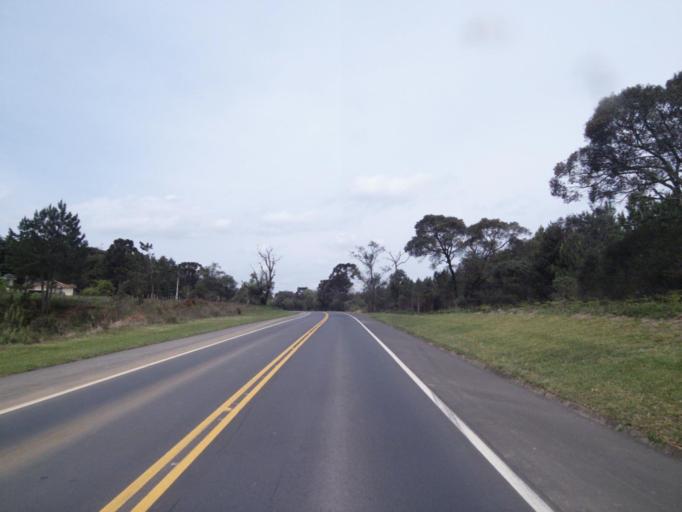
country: BR
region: Parana
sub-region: Irati
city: Irati
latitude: -25.4667
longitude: -50.5230
